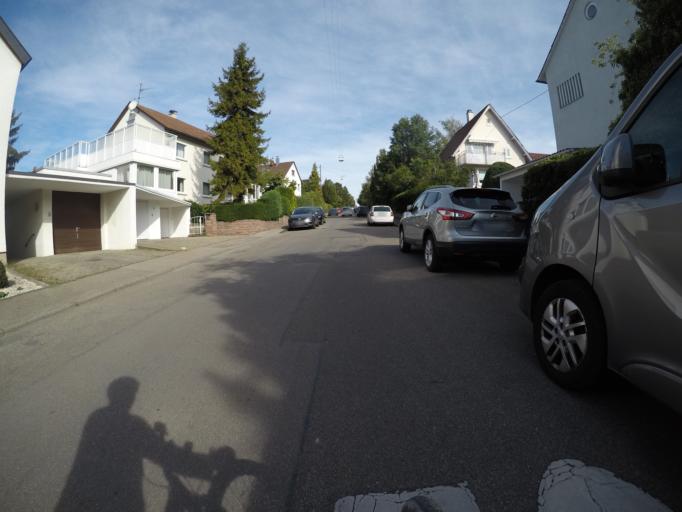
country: DE
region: Baden-Wuerttemberg
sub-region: Regierungsbezirk Stuttgart
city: Korntal
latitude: 48.8323
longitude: 9.1153
